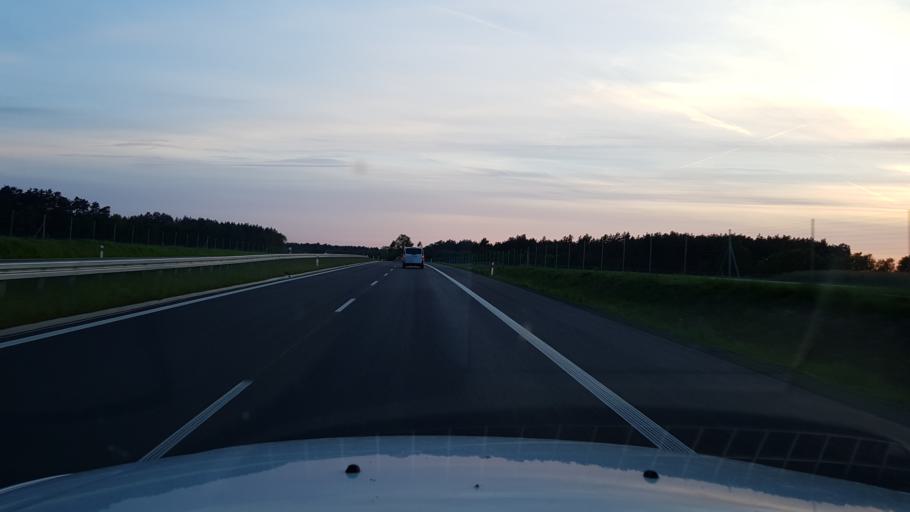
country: PL
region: West Pomeranian Voivodeship
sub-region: Powiat goleniowski
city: Osina
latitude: 53.6384
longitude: 15.0154
